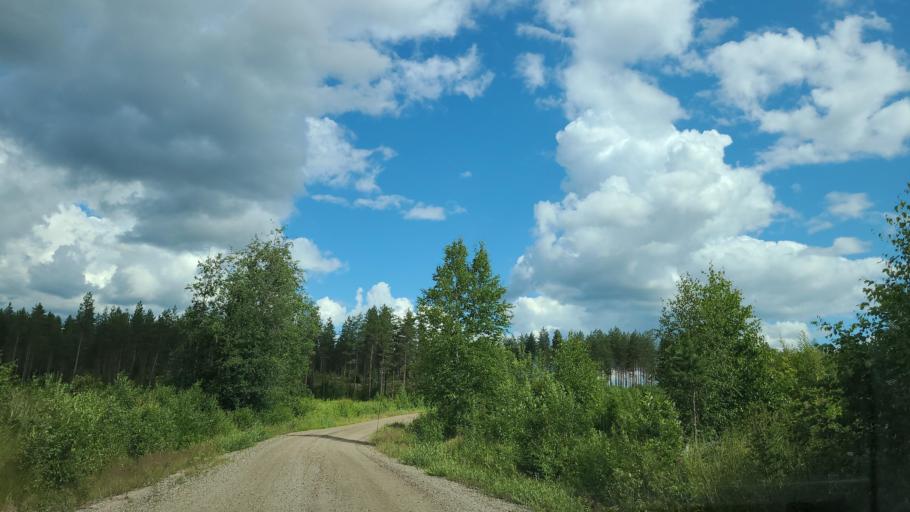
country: FI
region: Northern Savo
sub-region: Koillis-Savo
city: Kaavi
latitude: 63.0285
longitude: 28.7836
